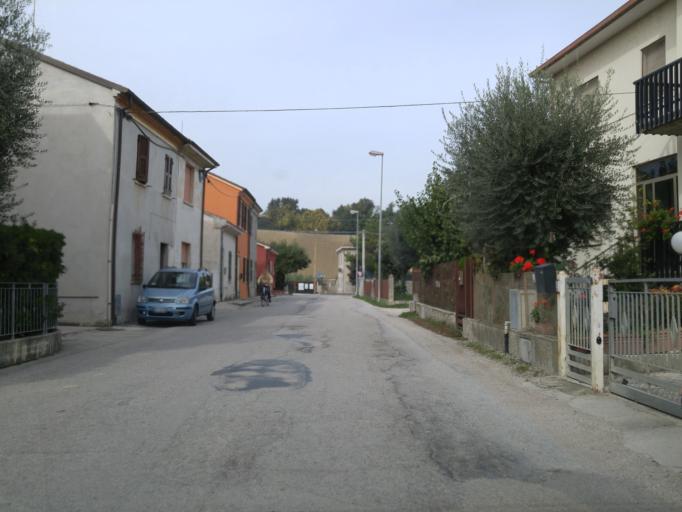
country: IT
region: The Marches
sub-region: Provincia di Pesaro e Urbino
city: Cuccurano
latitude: 43.7952
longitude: 12.9593
